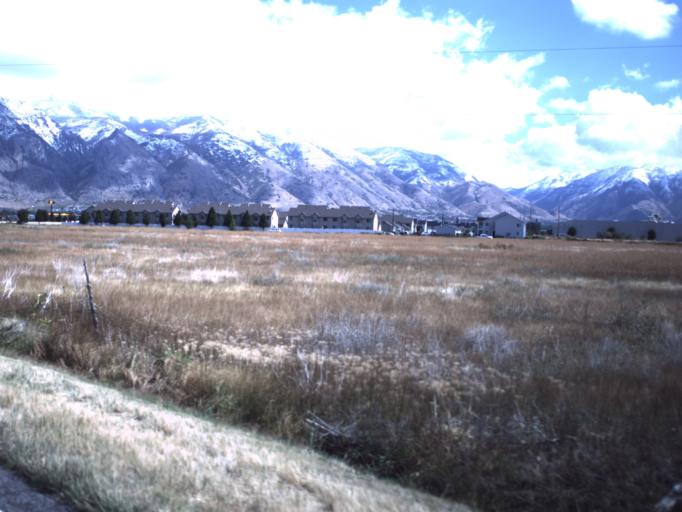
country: US
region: Utah
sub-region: Utah County
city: Spanish Fork
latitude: 40.1608
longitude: -111.6589
